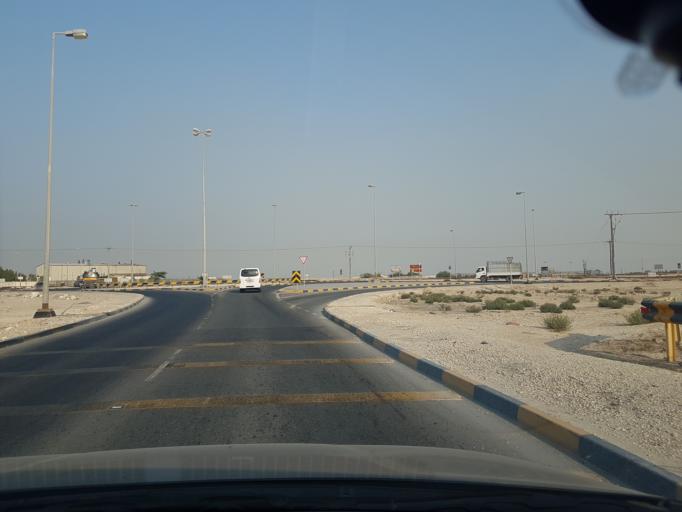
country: BH
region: Northern
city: Ar Rifa'
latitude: 26.0887
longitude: 50.5718
